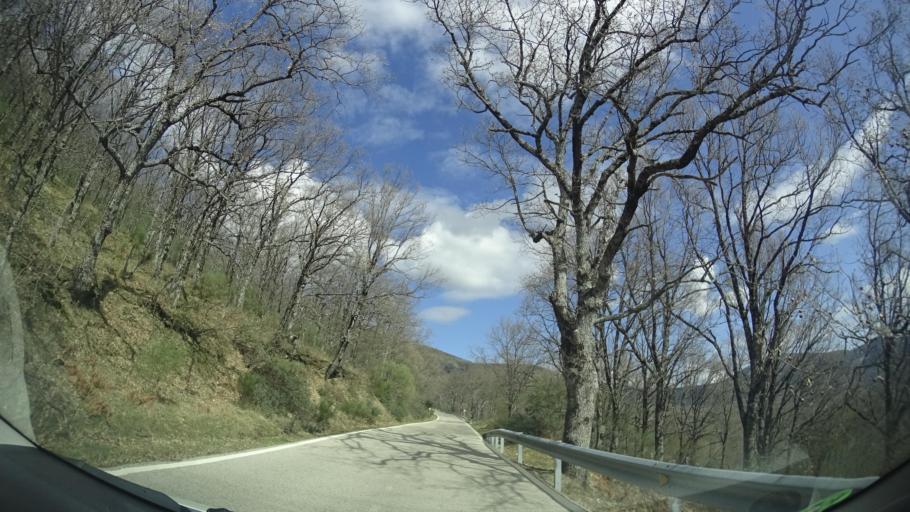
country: ES
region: Madrid
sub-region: Provincia de Madrid
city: Miraflores de la Sierra
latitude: 40.8253
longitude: -3.7630
